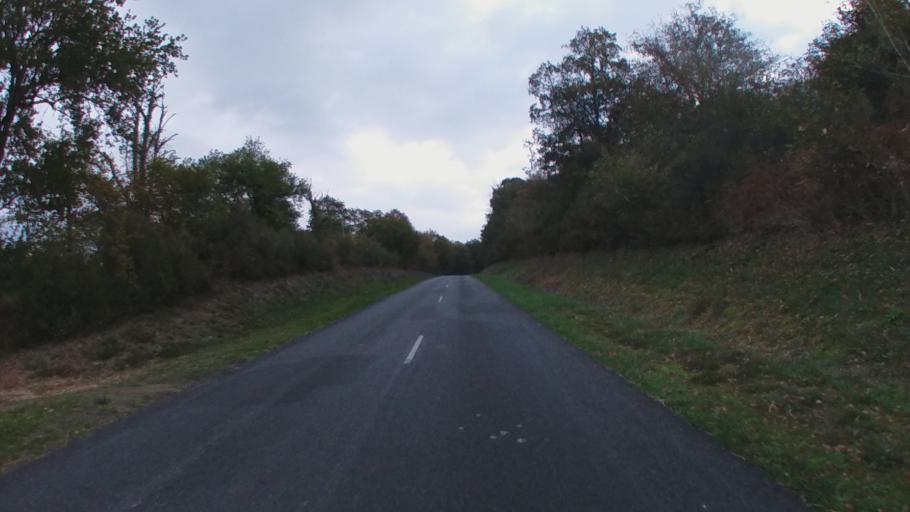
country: FR
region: Pays de la Loire
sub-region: Departement de Maine-et-Loire
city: Distre
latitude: 47.2595
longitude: -0.1228
